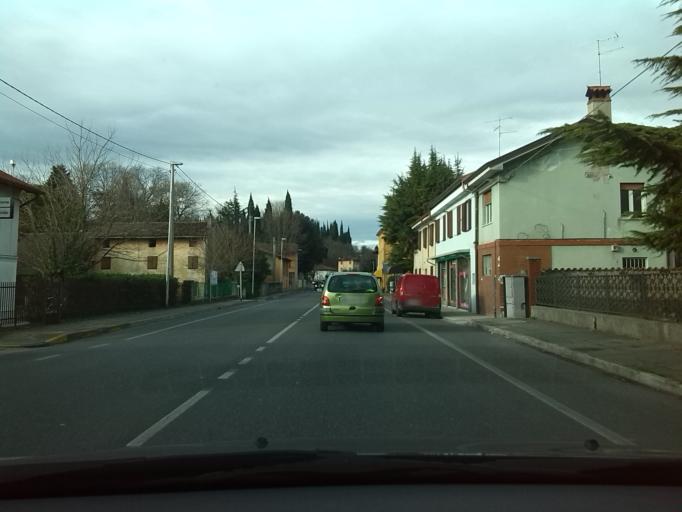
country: IT
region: Friuli Venezia Giulia
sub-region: Provincia di Gorizia
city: Fogliano
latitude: 45.8461
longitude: 13.4889
